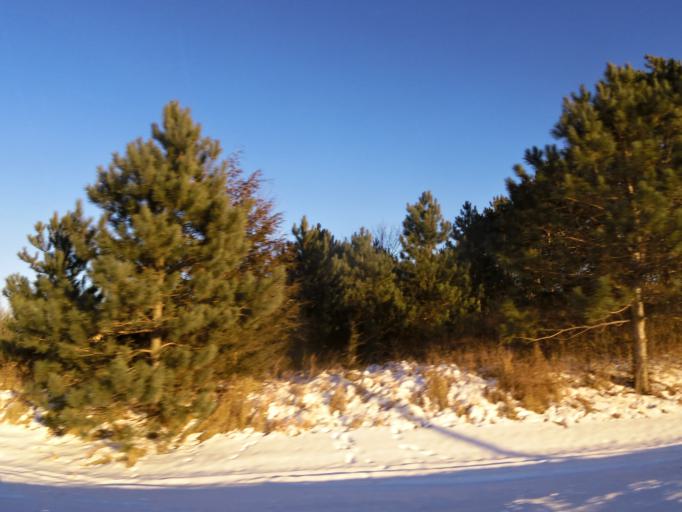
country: US
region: Minnesota
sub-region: Washington County
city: Bayport
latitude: 45.0637
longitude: -92.7409
